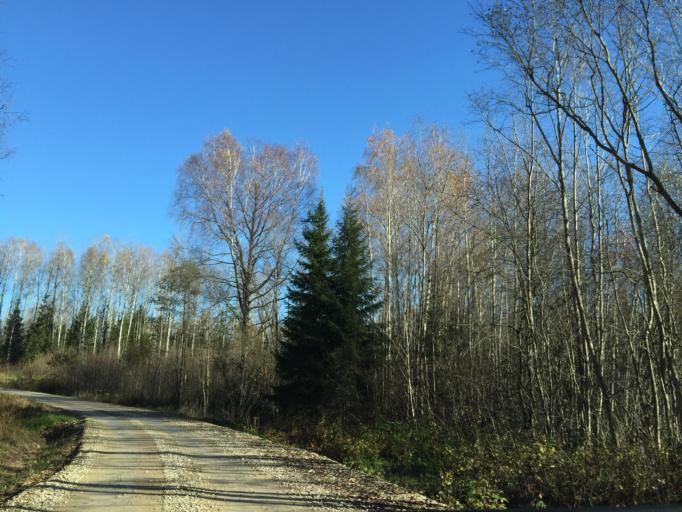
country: LV
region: Aizkraukles Rajons
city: Aizkraukle
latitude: 56.5758
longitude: 25.1802
